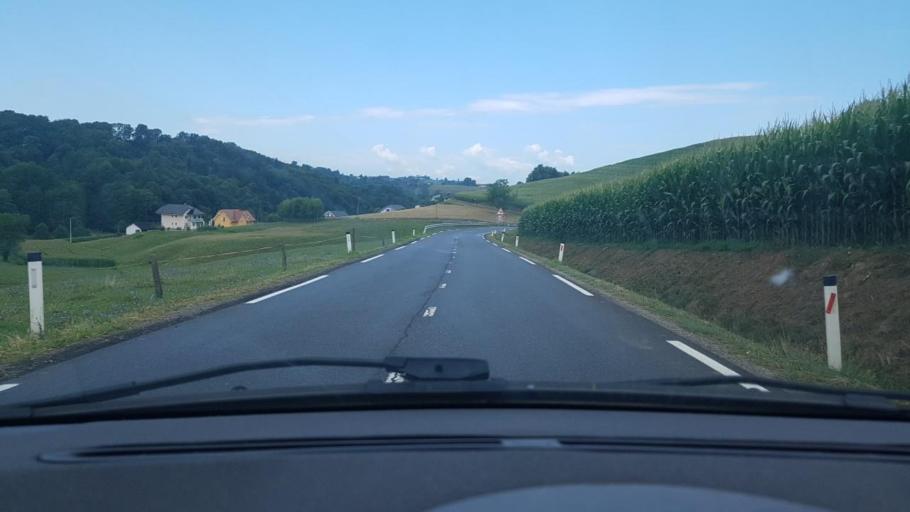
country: AT
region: Styria
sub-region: Politischer Bezirk Suedoststeiermark
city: Mureck
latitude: 46.6935
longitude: 15.7603
